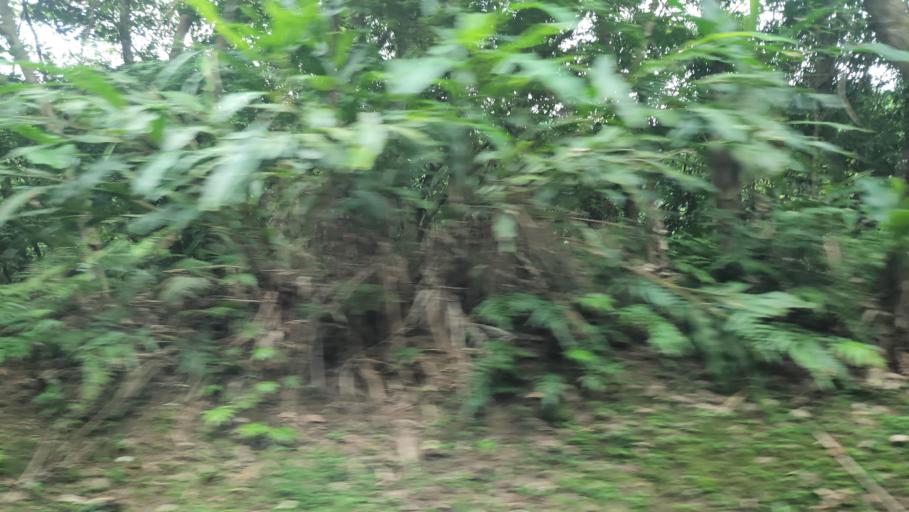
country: TW
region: Taipei
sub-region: Taipei
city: Banqiao
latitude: 24.8928
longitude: 121.4314
